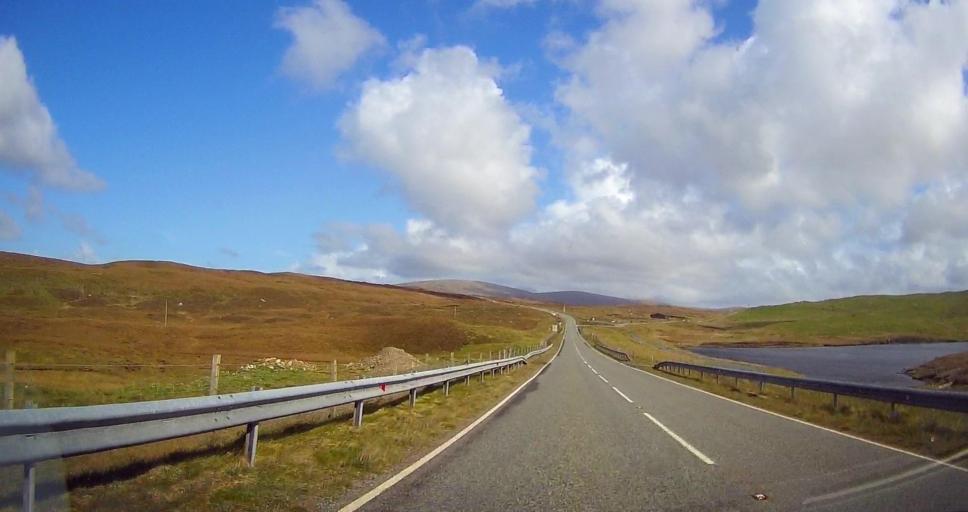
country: GB
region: Scotland
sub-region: Shetland Islands
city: Lerwick
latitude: 60.4720
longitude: -1.4070
